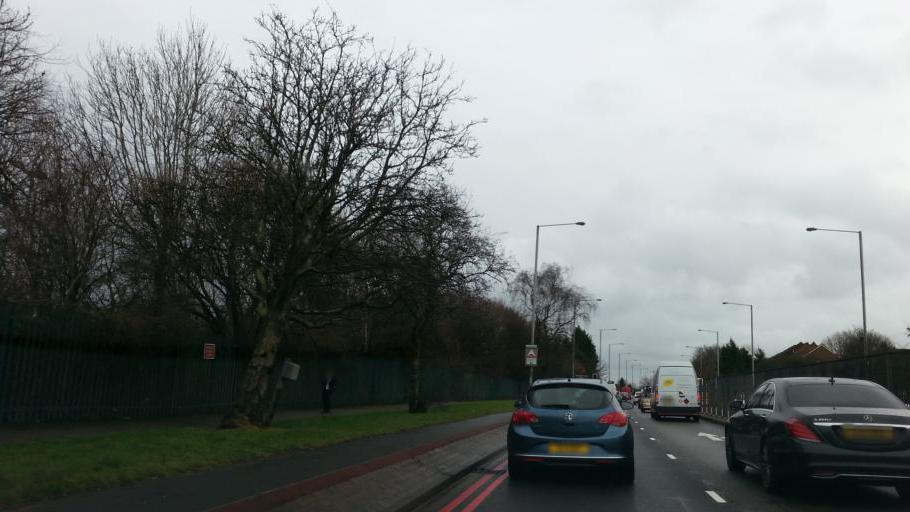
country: GB
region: England
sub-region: Sandwell
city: Rowley Regis
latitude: 52.5086
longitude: -2.0412
